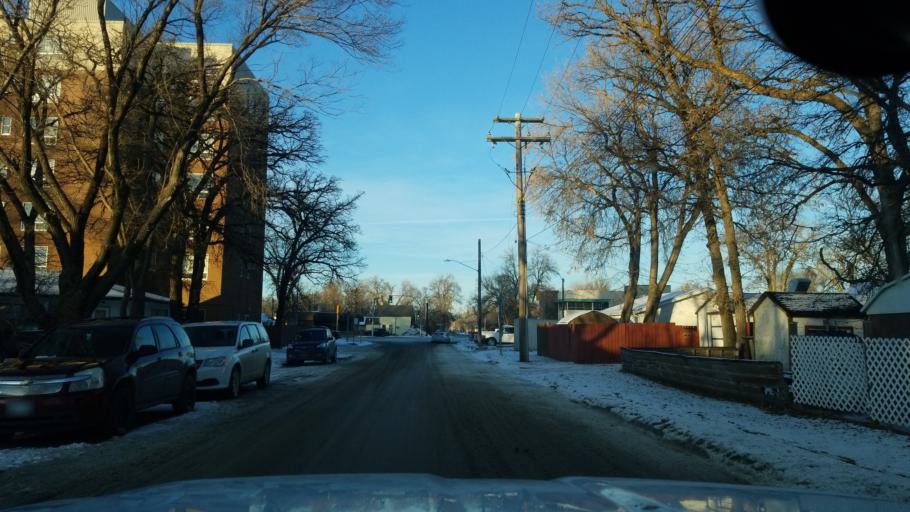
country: CA
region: Manitoba
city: Portage la Prairie
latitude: 49.9727
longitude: -98.3018
